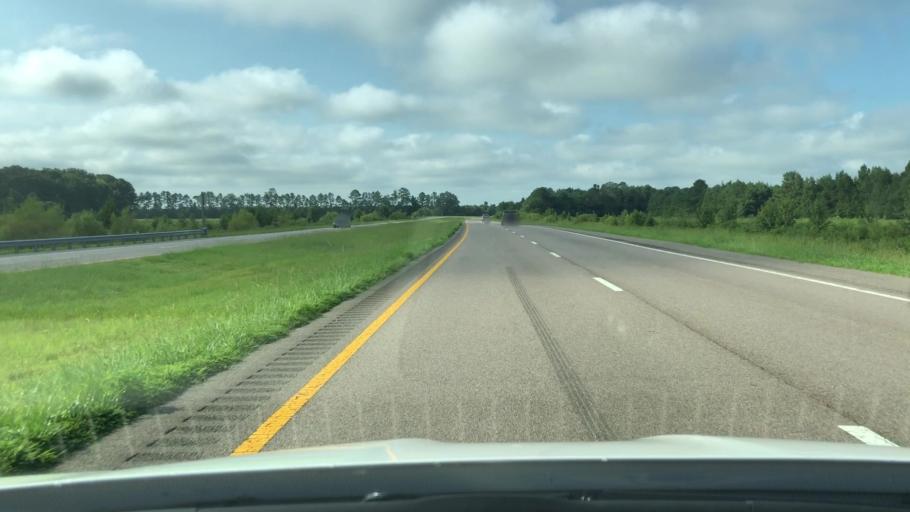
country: US
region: Virginia
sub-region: City of Portsmouth
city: Portsmouth Heights
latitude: 36.6842
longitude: -76.3475
